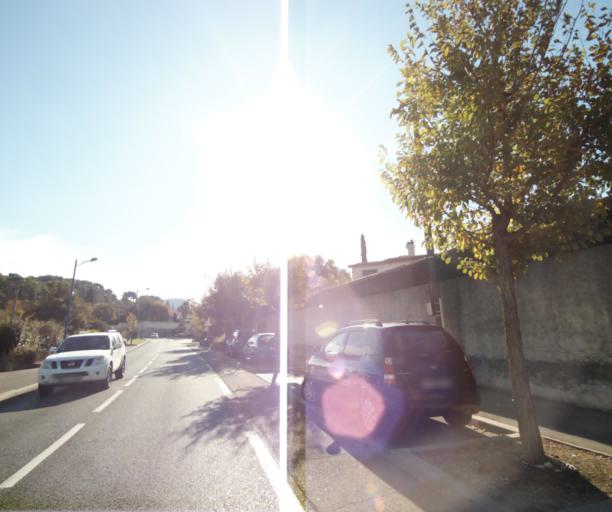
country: FR
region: Provence-Alpes-Cote d'Azur
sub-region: Departement des Bouches-du-Rhone
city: Allauch
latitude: 43.3542
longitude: 5.4872
